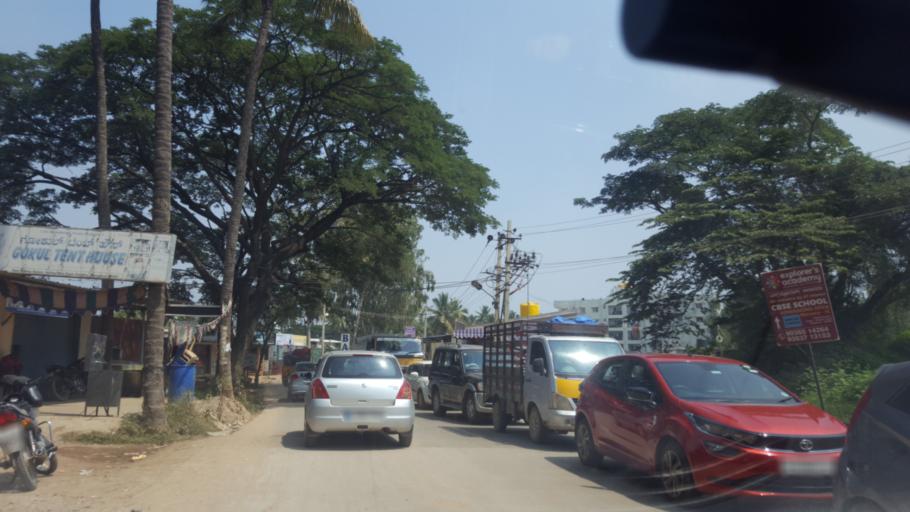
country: IN
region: Karnataka
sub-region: Bangalore Urban
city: Bangalore
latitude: 12.9360
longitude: 77.7079
